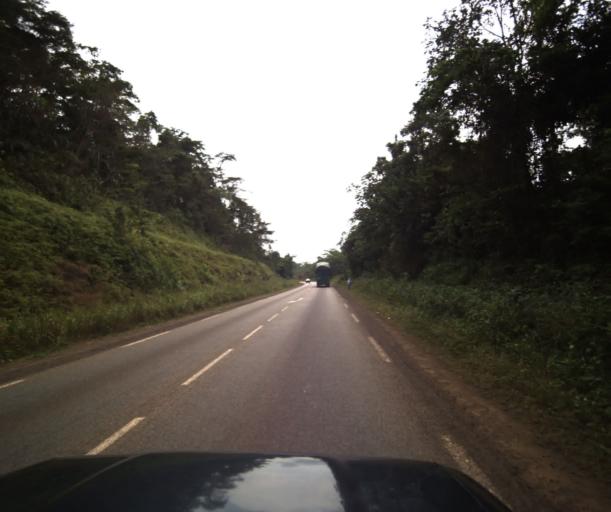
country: CM
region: Littoral
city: Edea
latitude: 3.8232
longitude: 10.3818
